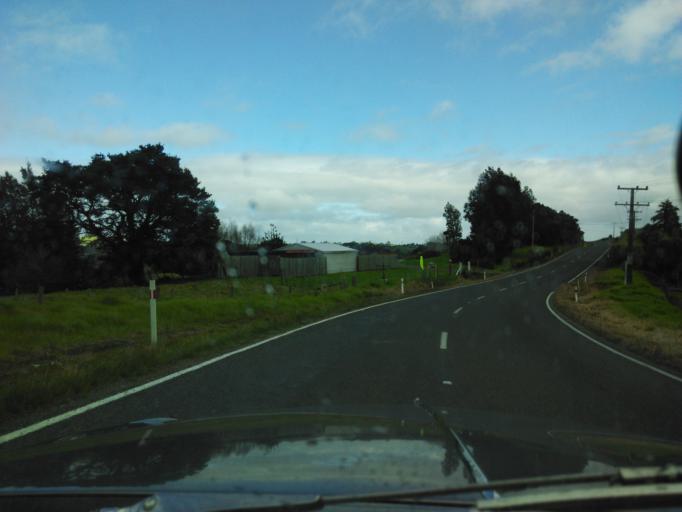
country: NZ
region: Auckland
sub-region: Auckland
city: Wellsford
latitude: -36.1584
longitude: 174.4583
